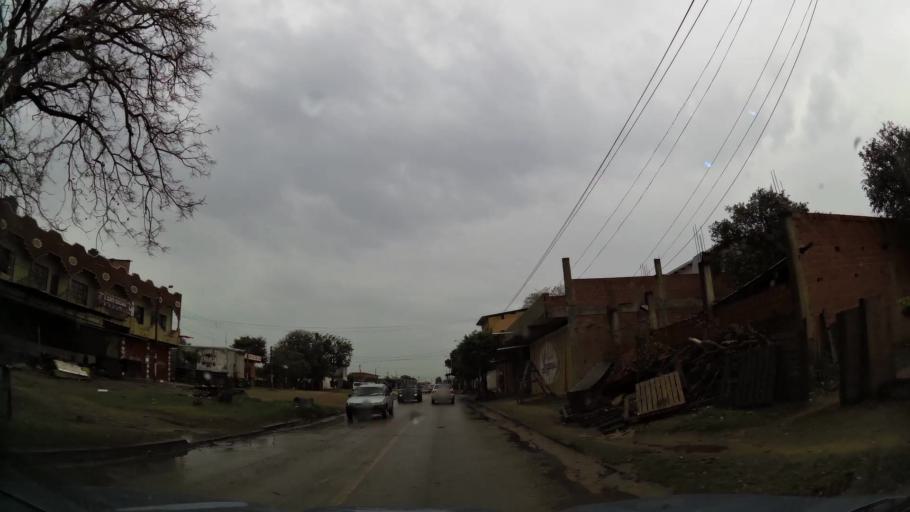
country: BO
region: Santa Cruz
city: Santa Cruz de la Sierra
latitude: -17.7605
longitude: -63.1240
